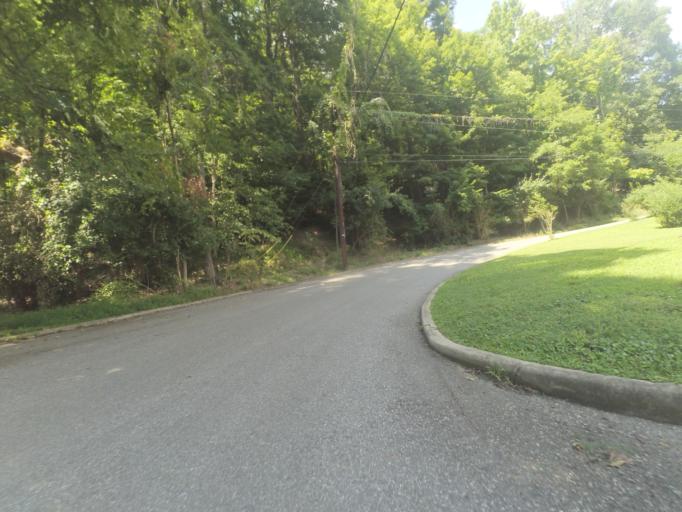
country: US
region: West Virginia
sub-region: Cabell County
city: Huntington
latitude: 38.3971
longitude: -82.4312
